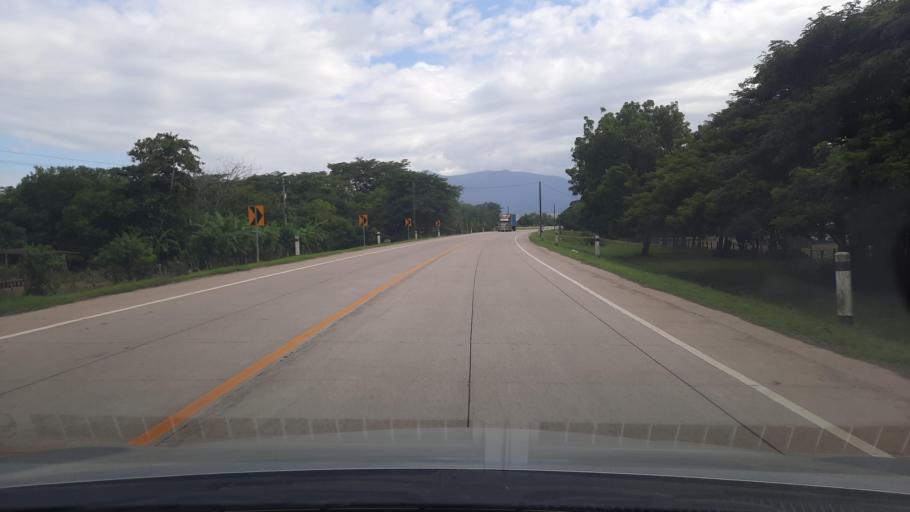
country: NI
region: Chinandega
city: Somotillo
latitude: 12.8178
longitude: -86.8996
